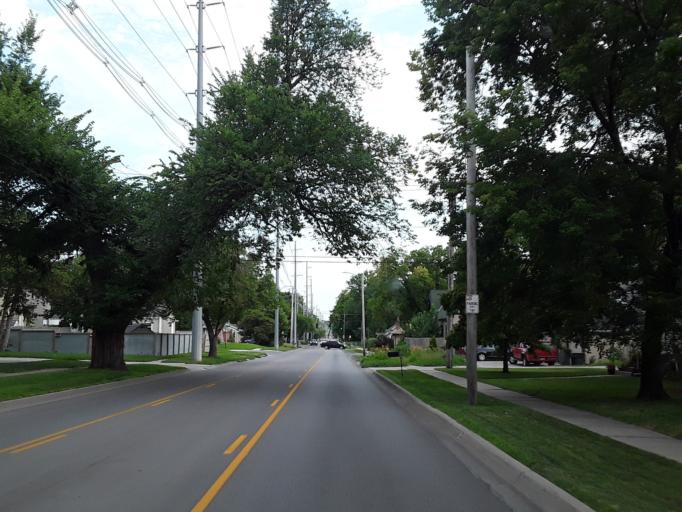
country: US
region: Nebraska
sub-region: Lancaster County
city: Lincoln
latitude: 40.8373
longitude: -96.6442
